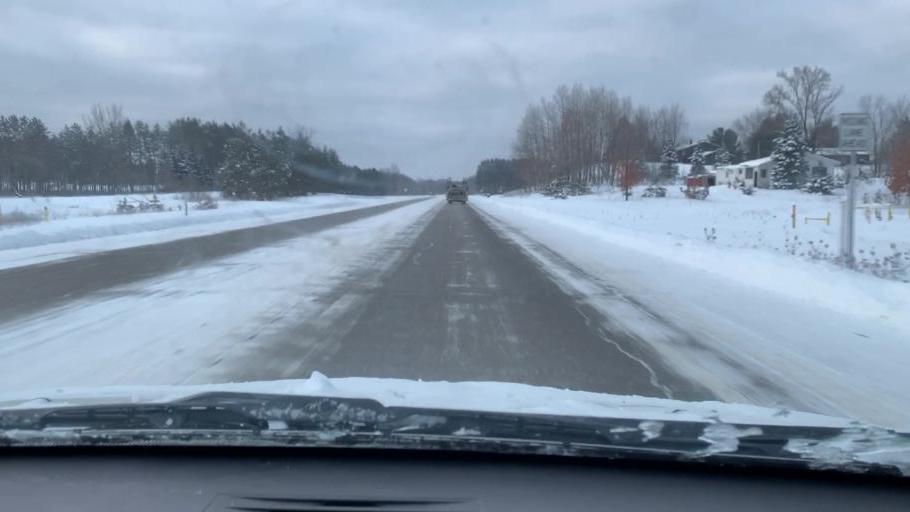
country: US
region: Michigan
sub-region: Kalkaska County
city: Kalkaska
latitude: 44.6234
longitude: -85.2977
